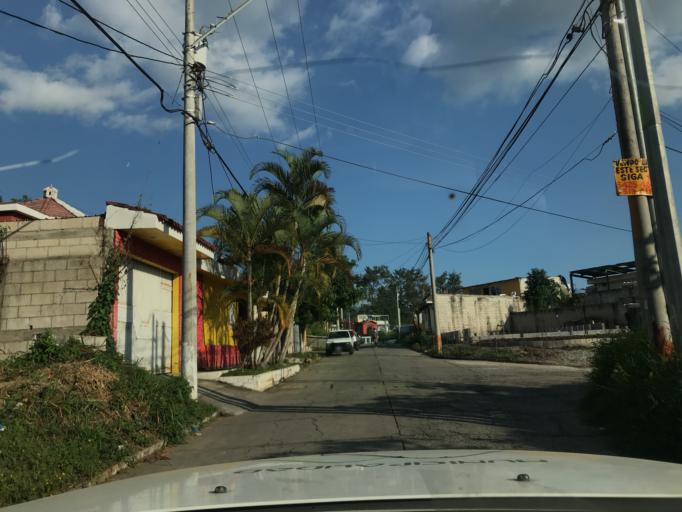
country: GT
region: Guatemala
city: Petapa
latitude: 14.4928
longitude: -90.5473
